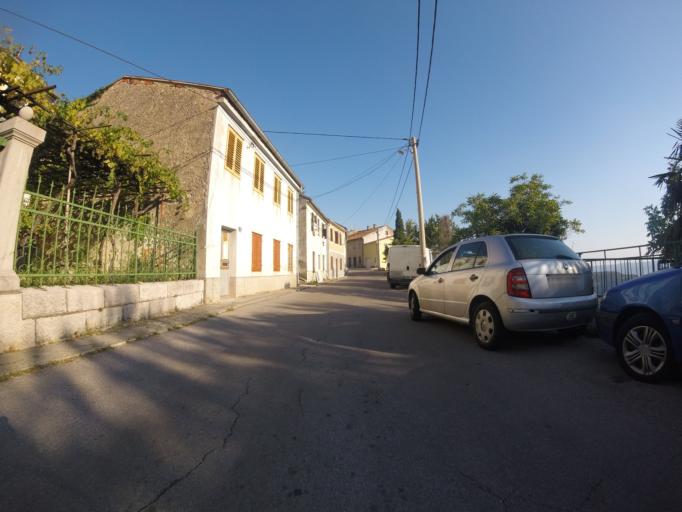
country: HR
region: Primorsko-Goranska
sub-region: Grad Crikvenica
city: Crikvenica
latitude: 45.2034
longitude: 14.7173
